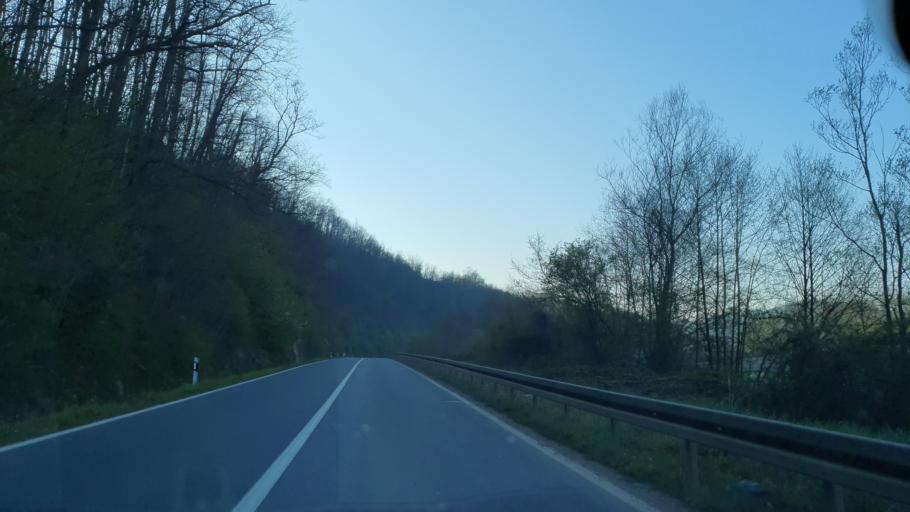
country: RS
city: Bukor
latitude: 44.4490
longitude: 19.4989
